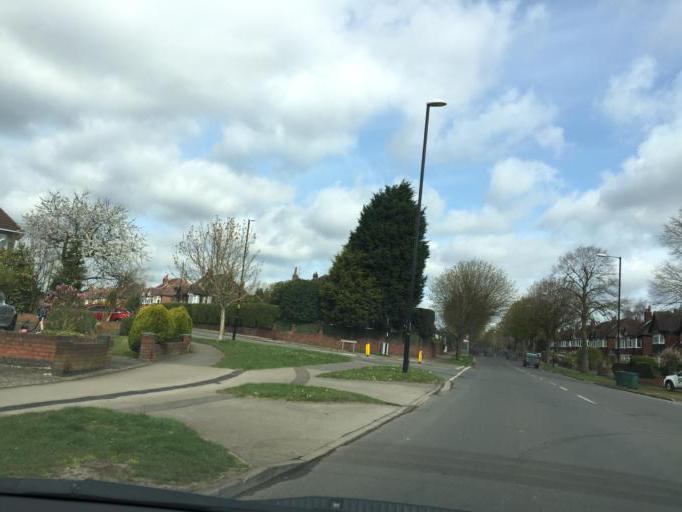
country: GB
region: England
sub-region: Coventry
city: Coventry
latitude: 52.3854
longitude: -1.5160
